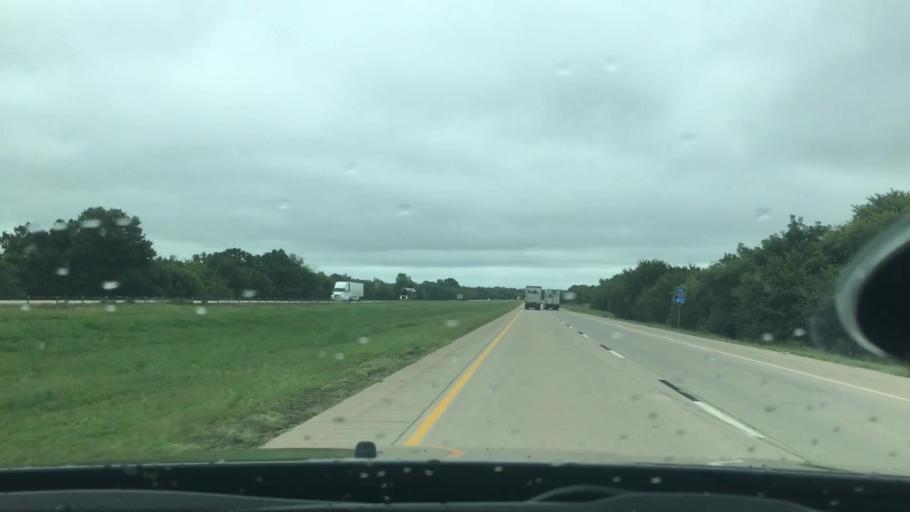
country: US
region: Oklahoma
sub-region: McIntosh County
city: Checotah
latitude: 35.4559
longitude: -95.6379
